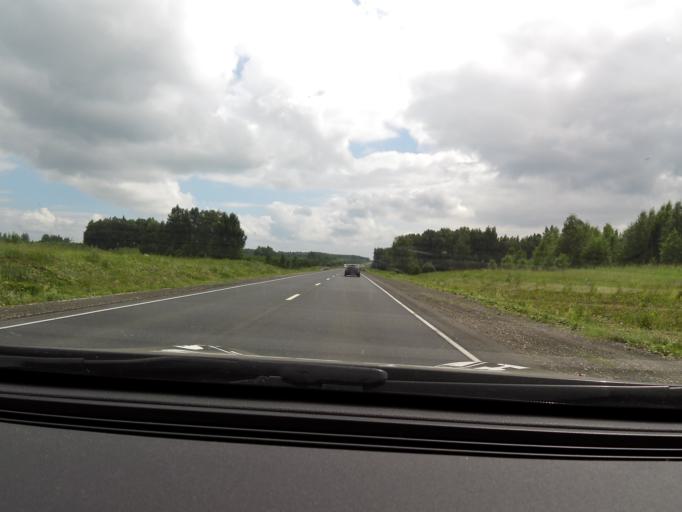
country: RU
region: Perm
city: Orda
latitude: 57.2385
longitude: 57.0588
